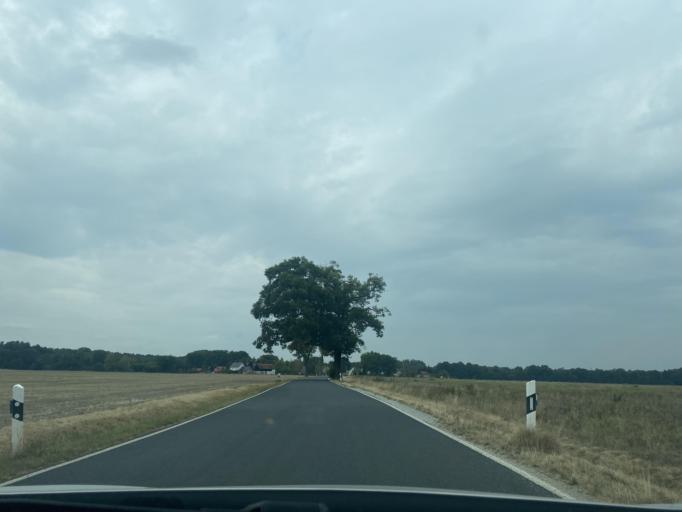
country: DE
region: Saxony
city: Konigswartha
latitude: 51.3065
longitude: 14.3762
